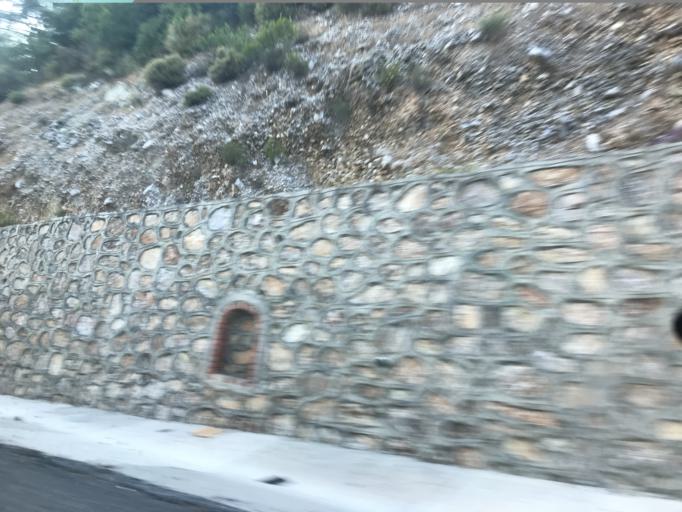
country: TR
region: Mugla
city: Yerkesik
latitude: 37.0612
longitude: 28.3435
